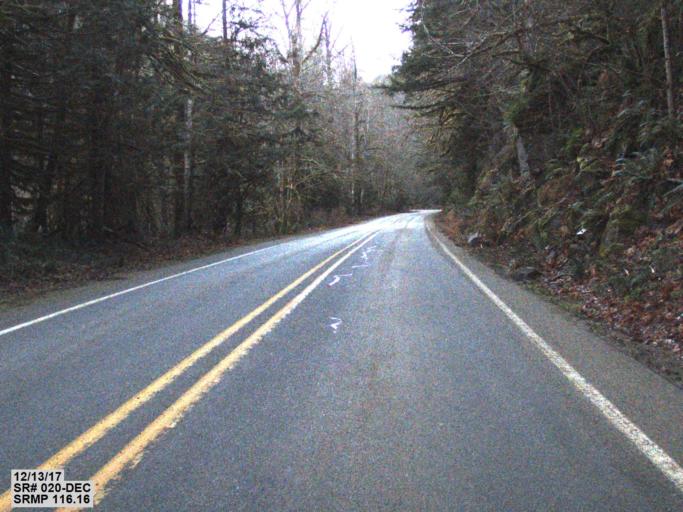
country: US
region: Washington
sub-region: Snohomish County
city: Darrington
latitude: 48.6374
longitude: -121.3174
